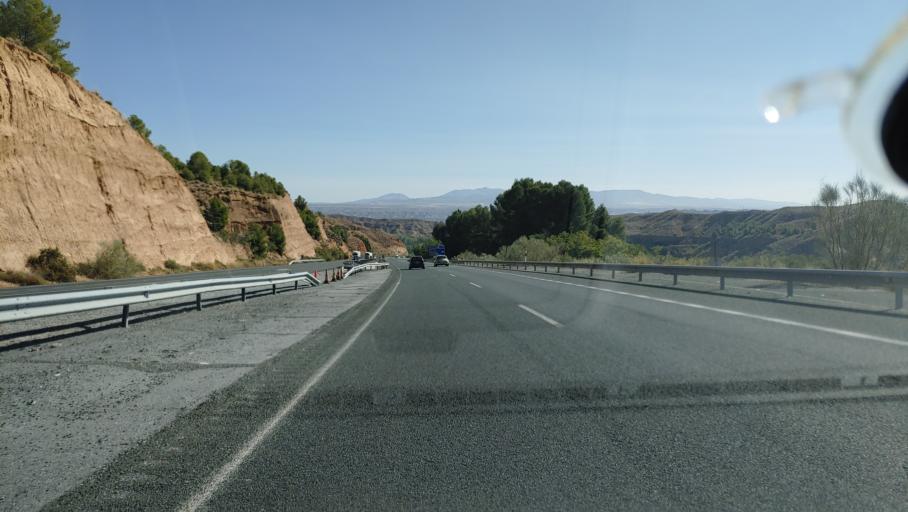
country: ES
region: Andalusia
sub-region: Provincia de Granada
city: Marchal
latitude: 37.3264
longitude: -3.2377
